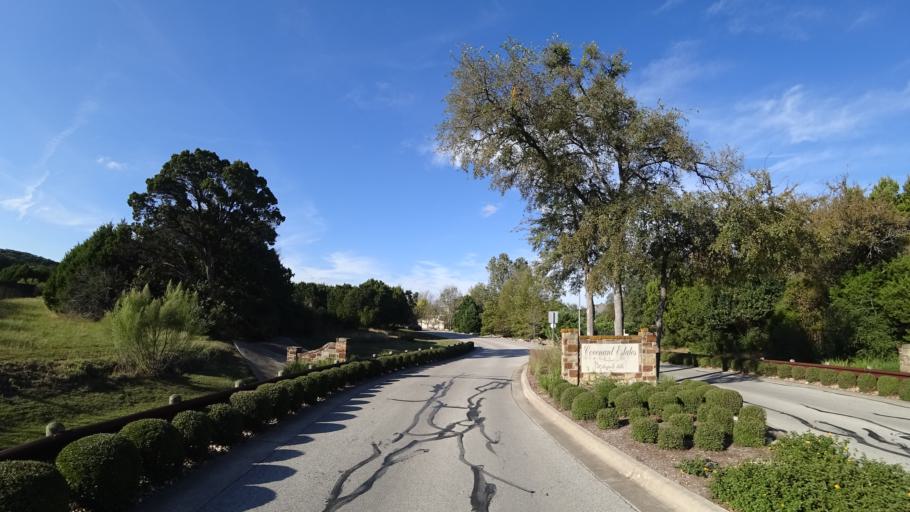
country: US
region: Texas
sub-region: Travis County
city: Lost Creek
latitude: 30.2599
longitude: -97.8424
